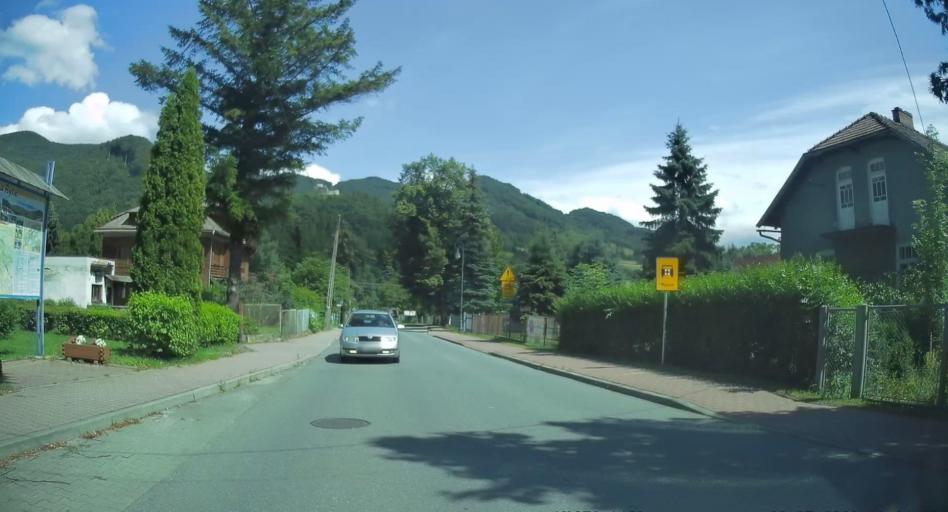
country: PL
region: Lesser Poland Voivodeship
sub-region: Powiat nowosadecki
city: Rytro
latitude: 49.4898
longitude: 20.6786
